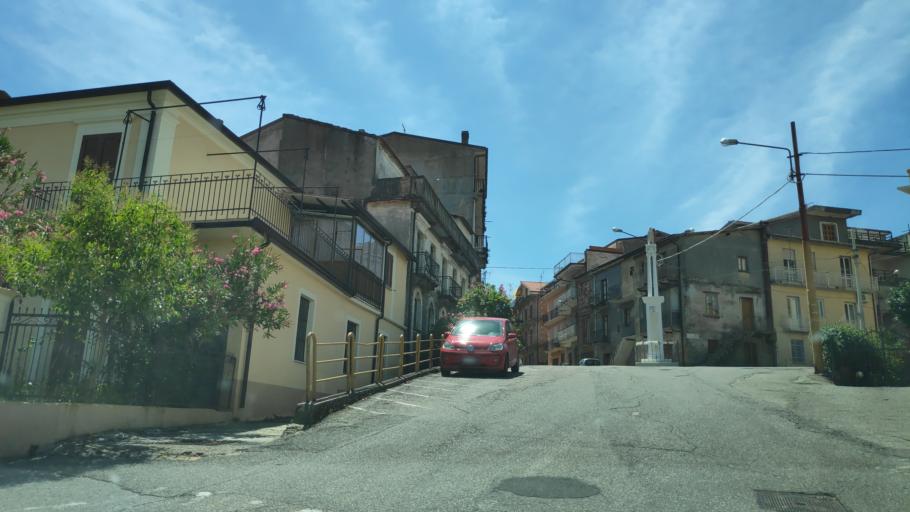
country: IT
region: Calabria
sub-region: Provincia di Catanzaro
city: Palermiti
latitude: 38.7493
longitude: 16.4536
